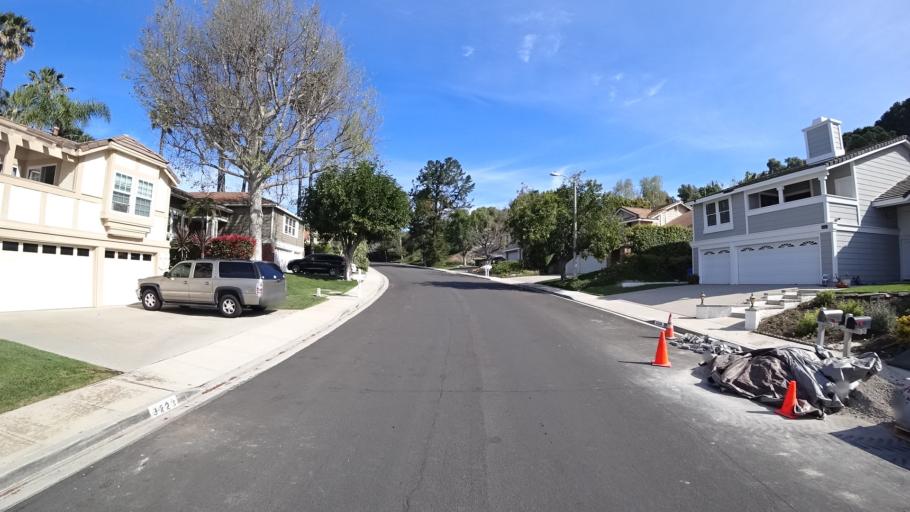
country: US
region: California
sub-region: Ventura County
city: Thousand Oaks
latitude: 34.2233
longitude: -118.8390
